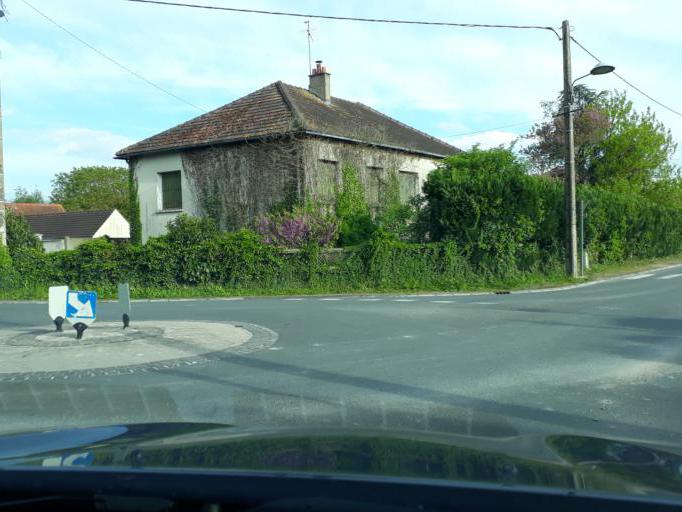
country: FR
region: Centre
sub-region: Departement du Loiret
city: Ingre
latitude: 47.9114
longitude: 1.8446
